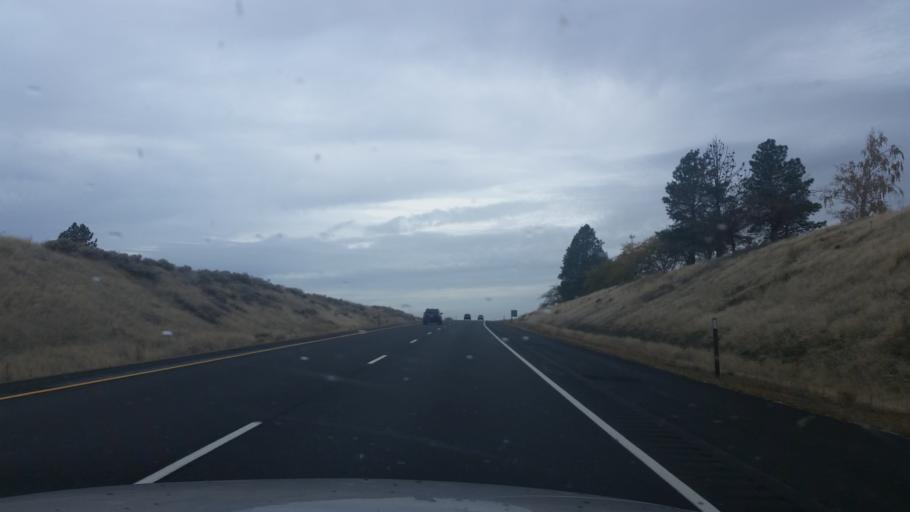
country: US
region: Washington
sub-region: Grant County
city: Warden
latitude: 47.0862
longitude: -118.8437
